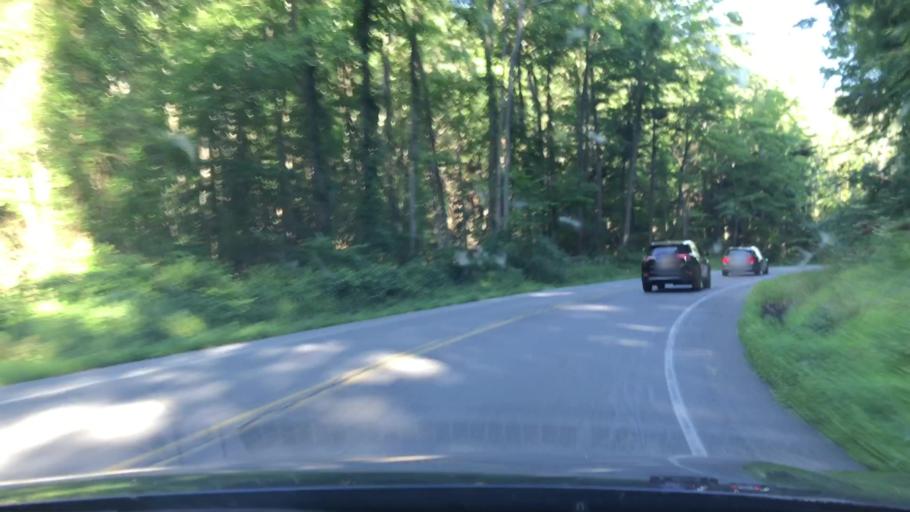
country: US
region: New York
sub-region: Putnam County
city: Mahopac
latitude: 41.3748
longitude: -73.7008
